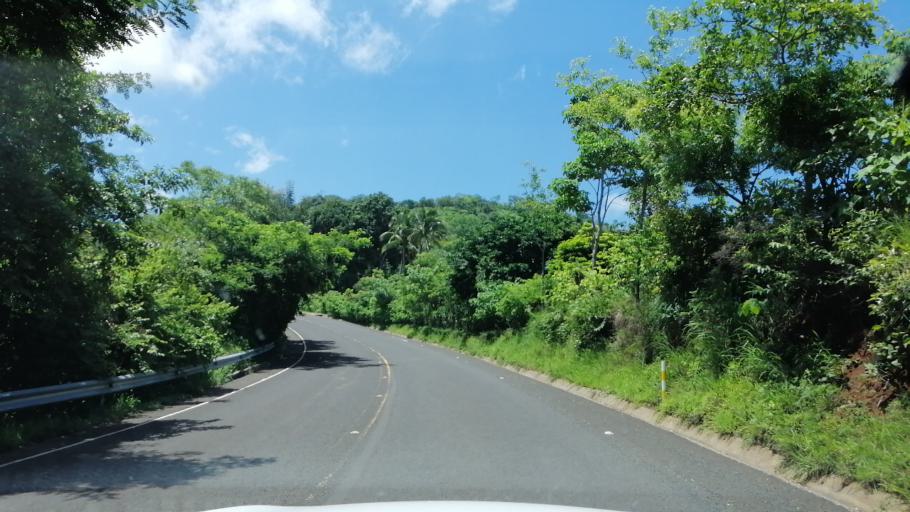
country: SV
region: San Miguel
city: Ciudad Barrios
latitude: 13.8019
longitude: -88.2988
